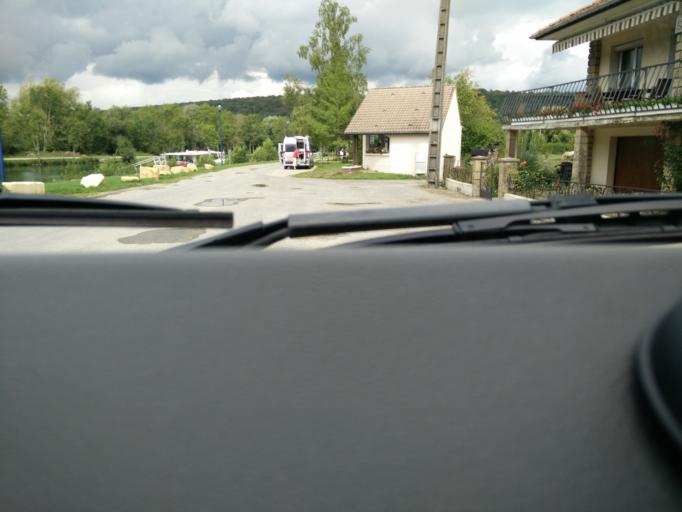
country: FR
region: Lorraine
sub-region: Departement de la Meuse
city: Stenay
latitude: 49.3880
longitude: 5.1790
